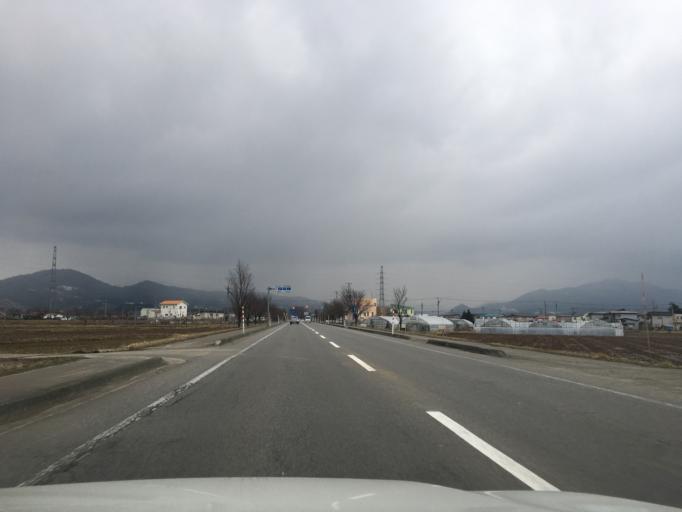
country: JP
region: Aomori
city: Kuroishi
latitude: 40.5778
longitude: 140.5684
